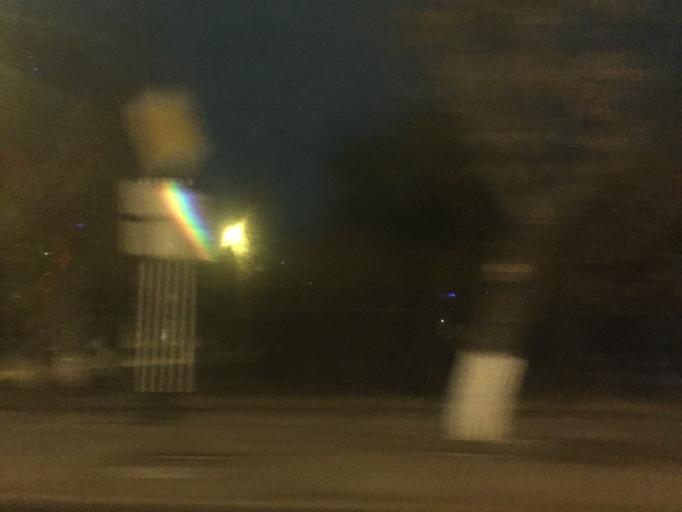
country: KZ
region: Astana Qalasy
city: Astana
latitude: 51.1627
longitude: 71.4177
